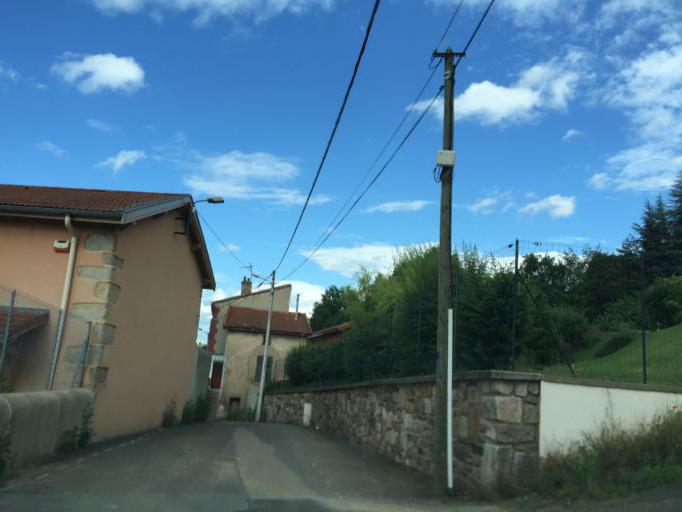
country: FR
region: Rhone-Alpes
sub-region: Departement de la Loire
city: Saint-Jean-Bonnefonds
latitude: 45.4401
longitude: 4.4716
